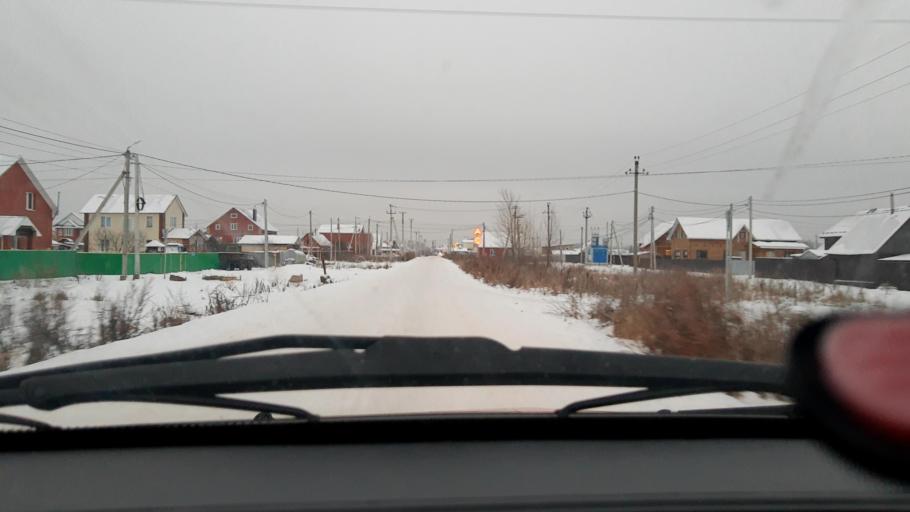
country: RU
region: Bashkortostan
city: Mikhaylovka
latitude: 54.7904
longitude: 55.8232
